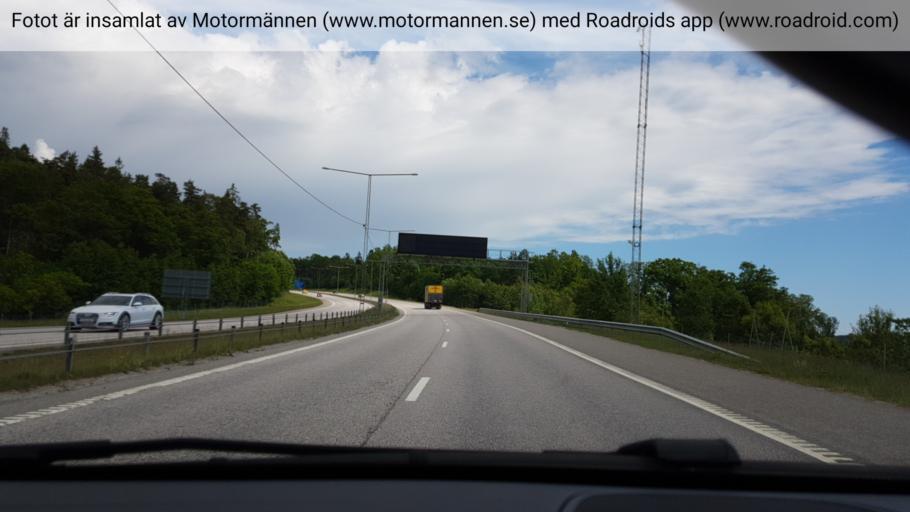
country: SE
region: Stockholm
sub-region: Haninge Kommun
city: Haninge
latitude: 59.1352
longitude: 18.1558
